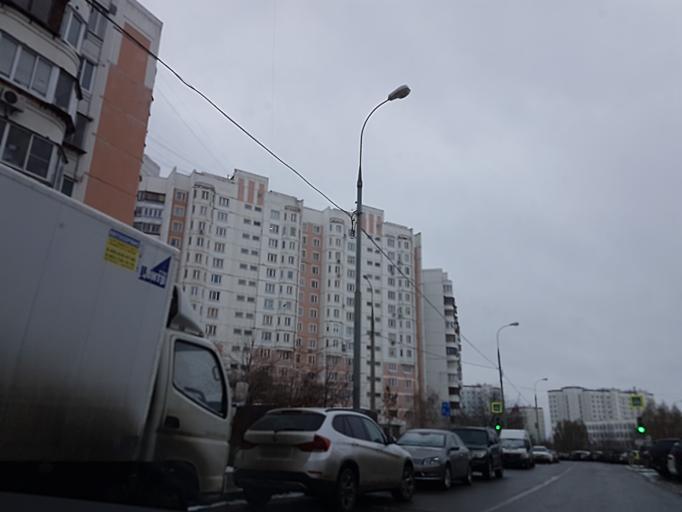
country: RU
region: Moskovskaya
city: Pavshino
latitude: 55.8310
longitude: 37.3505
